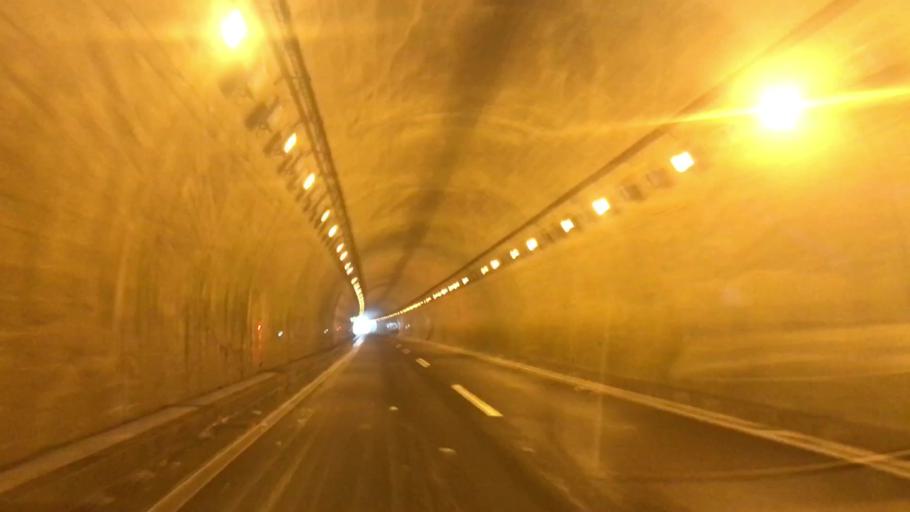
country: JP
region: Hokkaido
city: Muroran
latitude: 42.4241
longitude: 141.0898
